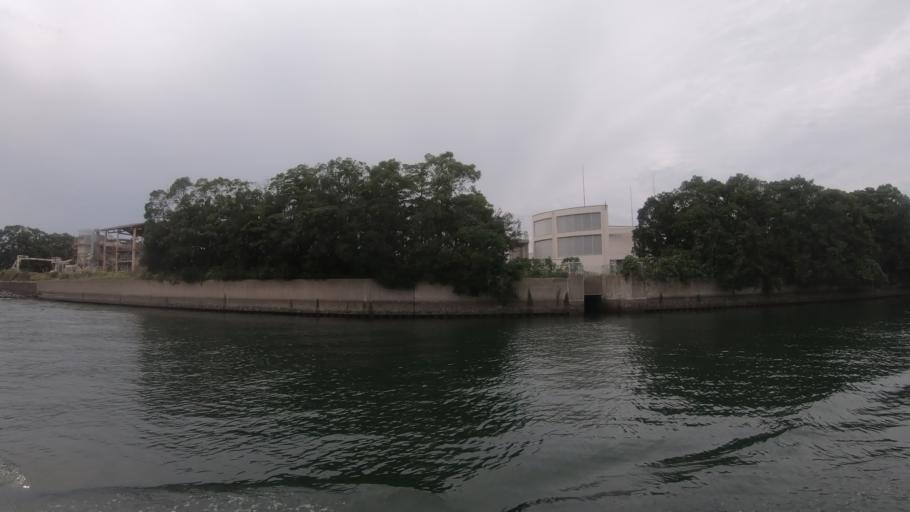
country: JP
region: Kanagawa
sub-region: Kawasaki-shi
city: Kawasaki
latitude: 35.4901
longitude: 139.6888
